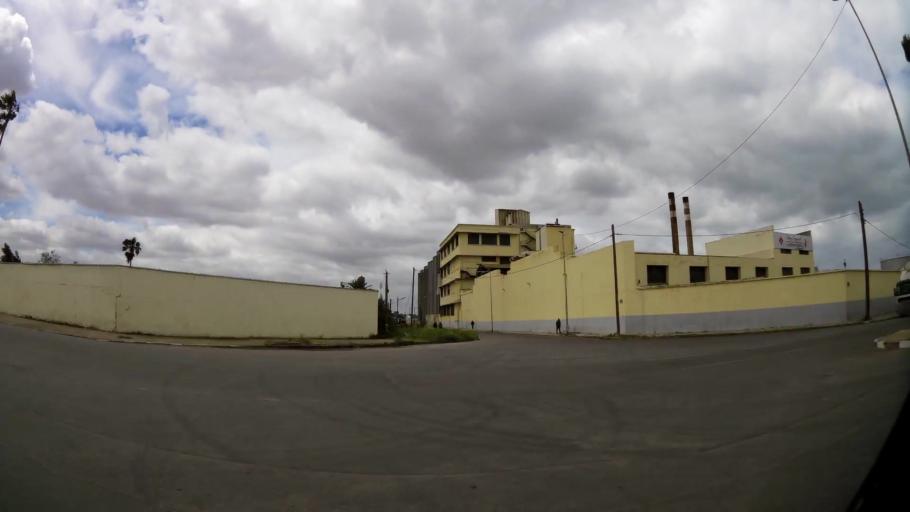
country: MA
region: Grand Casablanca
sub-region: Casablanca
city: Casablanca
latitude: 33.6071
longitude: -7.5637
